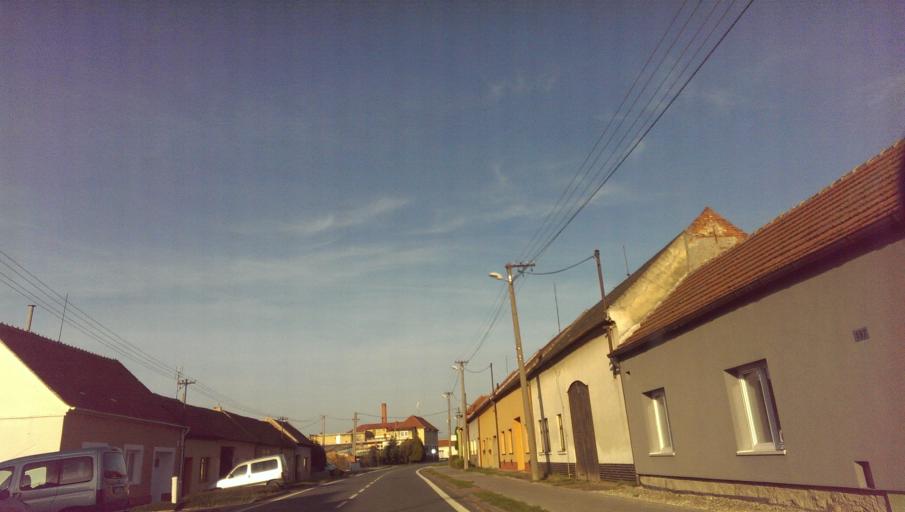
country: CZ
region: Zlin
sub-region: Okres Zlin
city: Ostrozska Nova Ves
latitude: 48.9987
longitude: 17.4303
